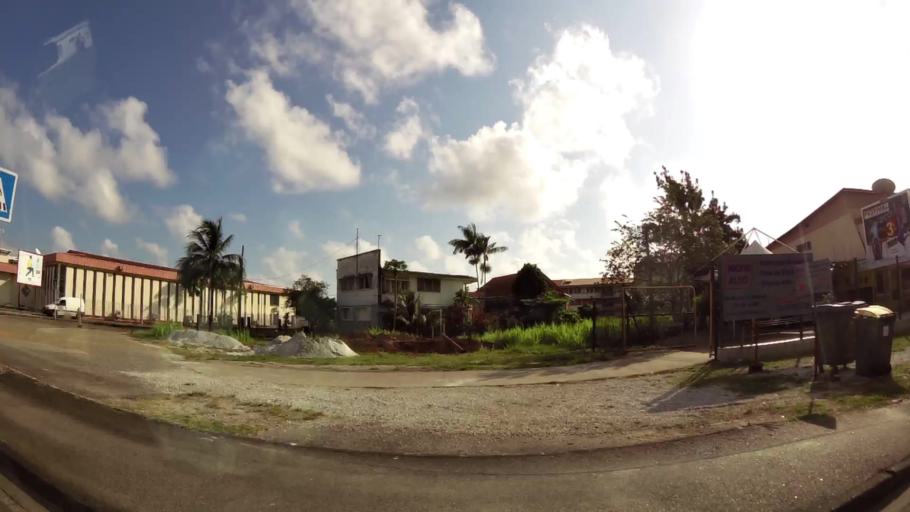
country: GF
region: Guyane
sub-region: Guyane
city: Cayenne
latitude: 4.9412
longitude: -52.3210
